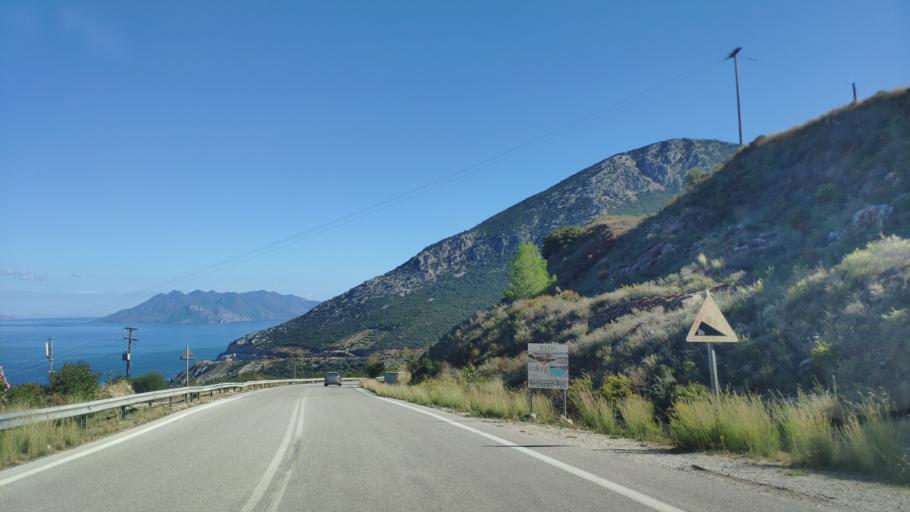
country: GR
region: Peloponnese
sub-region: Nomos Argolidos
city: Palaia Epidavros
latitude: 37.6110
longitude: 23.1529
